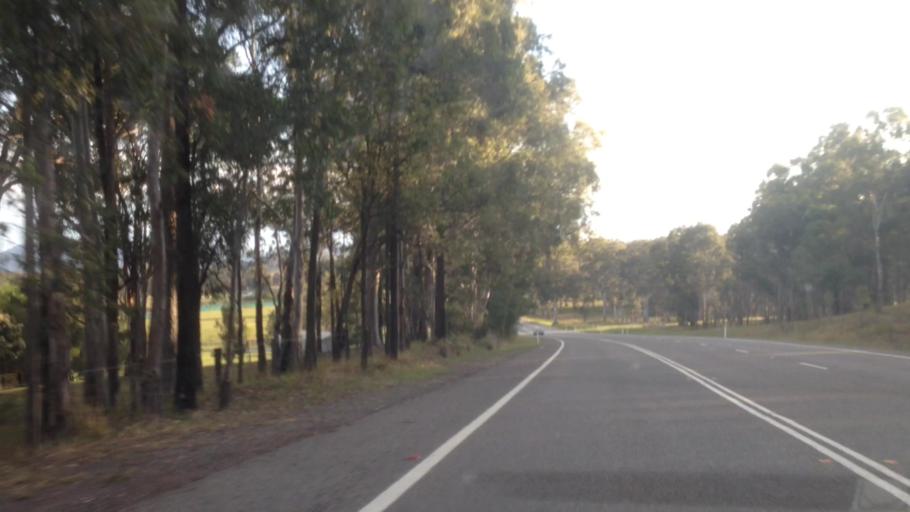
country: AU
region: New South Wales
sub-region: Cessnock
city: Kurri Kurri
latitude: -32.8617
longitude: 151.4827
